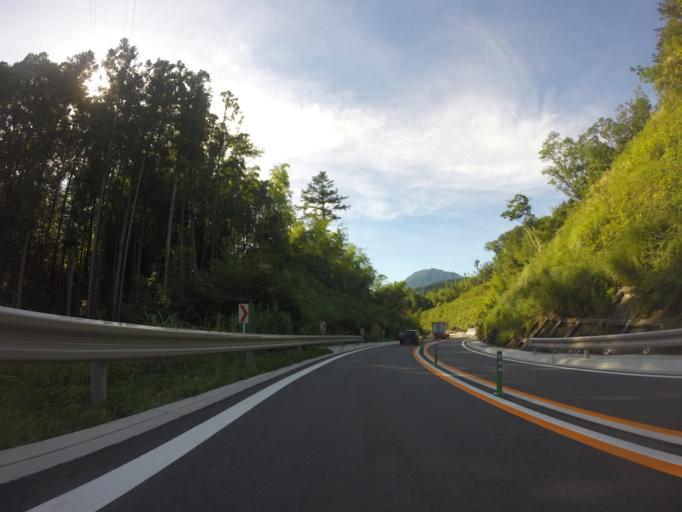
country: JP
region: Shizuoka
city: Fujinomiya
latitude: 35.2512
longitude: 138.4755
